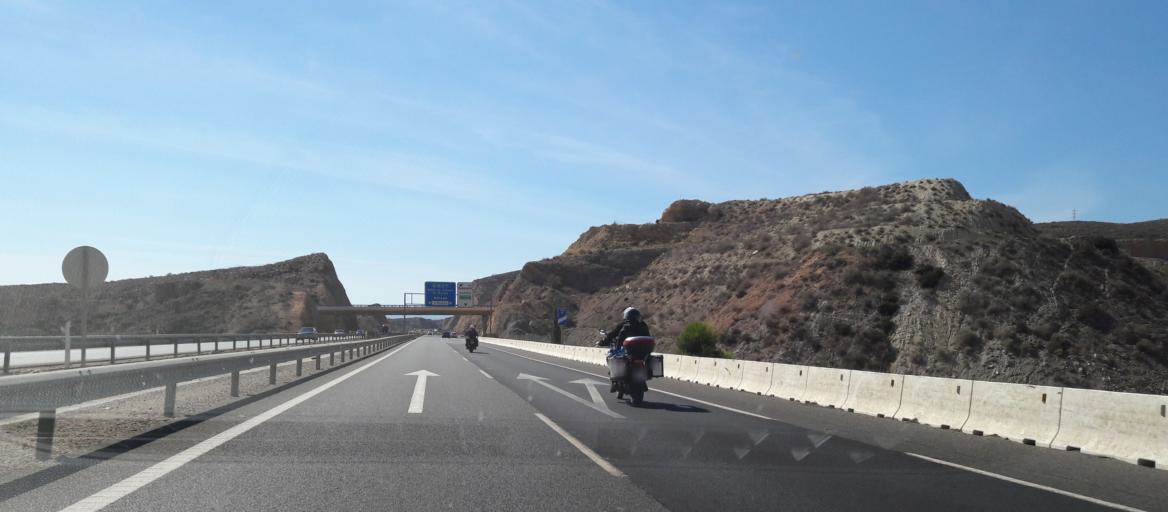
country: ES
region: Andalusia
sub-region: Provincia de Almeria
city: Huercal de Almeria
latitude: 36.8765
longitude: -2.4598
